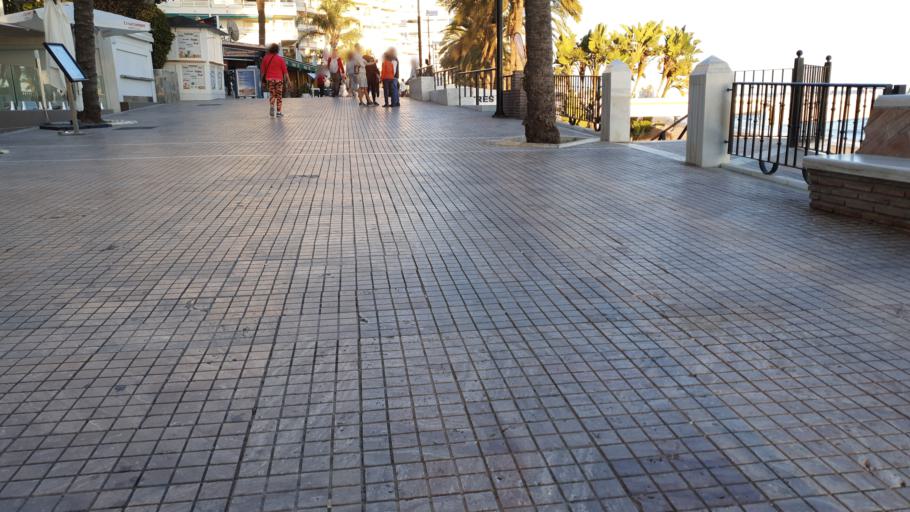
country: ES
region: Andalusia
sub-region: Provincia de Malaga
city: Marbella
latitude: 36.5071
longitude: -4.8966
